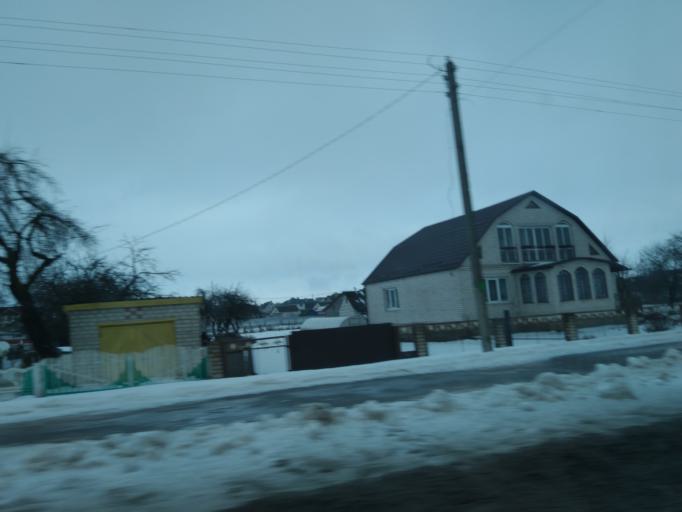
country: BY
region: Minsk
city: Nyasvizh
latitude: 53.2280
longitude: 26.6638
